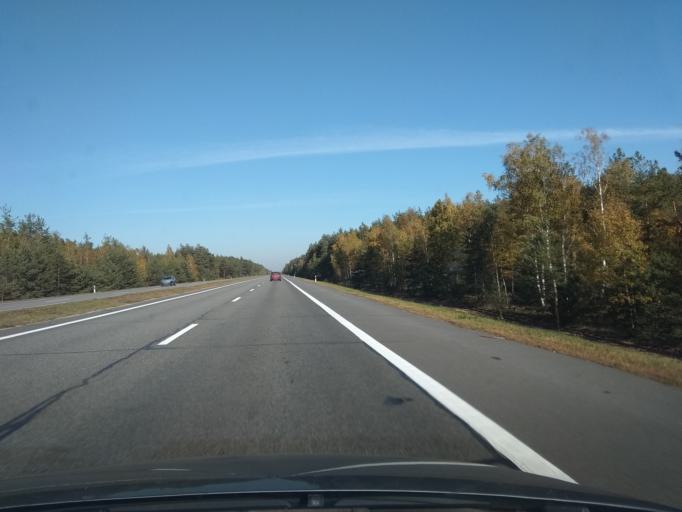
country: BY
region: Grodnenskaya
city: Zhyrovichy
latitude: 52.9298
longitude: 25.6960
